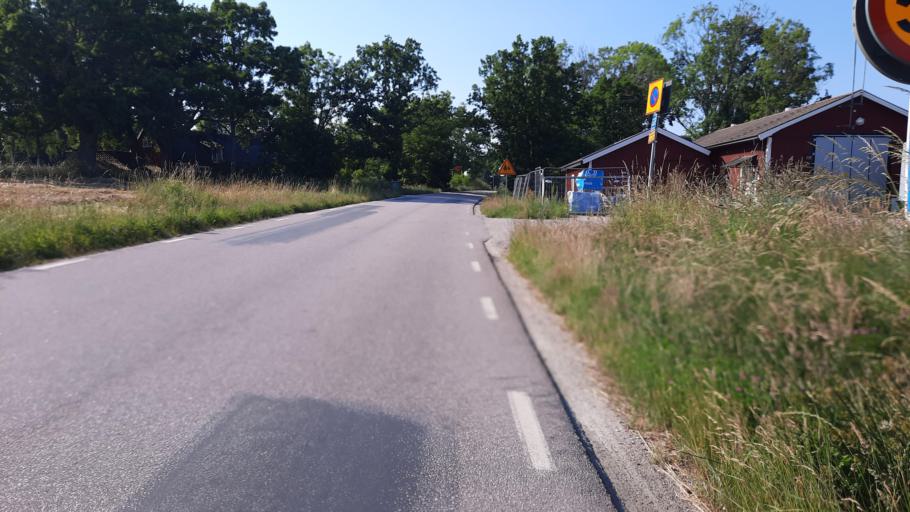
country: SE
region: Blekinge
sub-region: Karlskrona Kommun
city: Sturko
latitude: 56.1104
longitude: 15.6823
